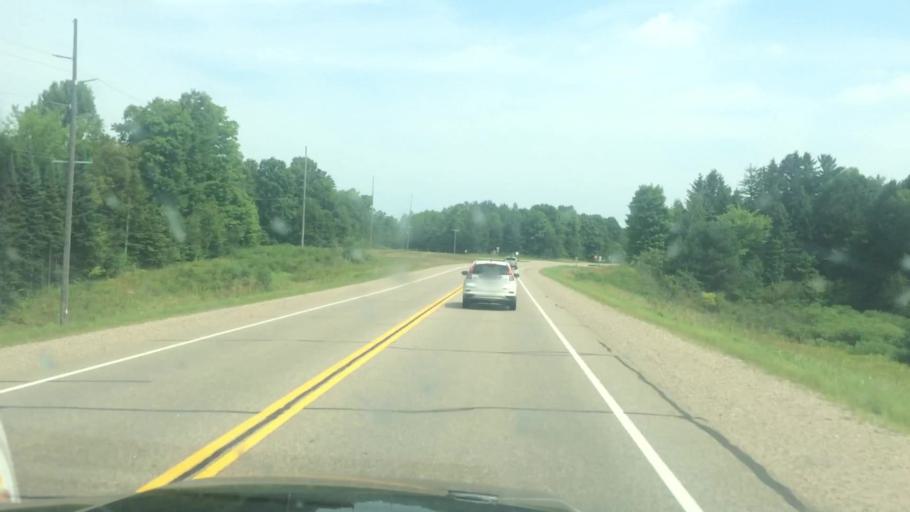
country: US
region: Wisconsin
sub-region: Langlade County
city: Antigo
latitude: 45.1651
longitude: -89.0125
